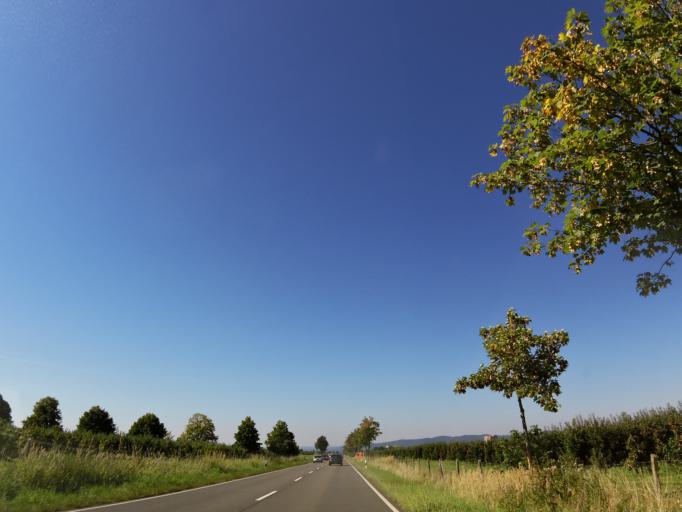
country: DE
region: Saxony
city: Pirna
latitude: 50.9397
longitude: 13.9645
